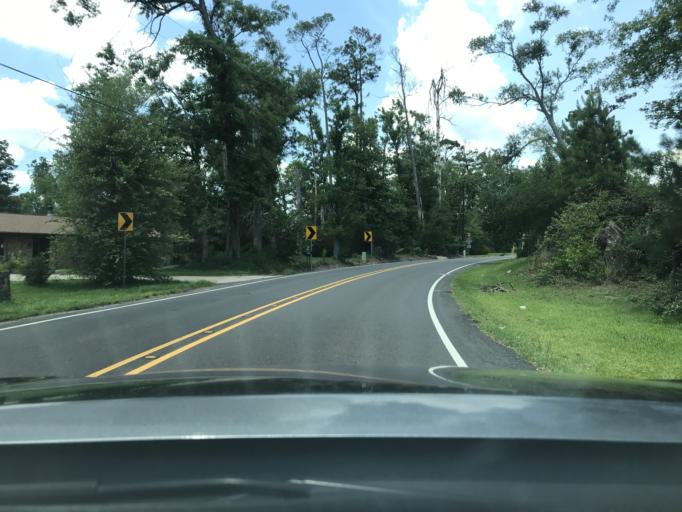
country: US
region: Louisiana
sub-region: Calcasieu Parish
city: Moss Bluff
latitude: 30.3140
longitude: -93.1852
